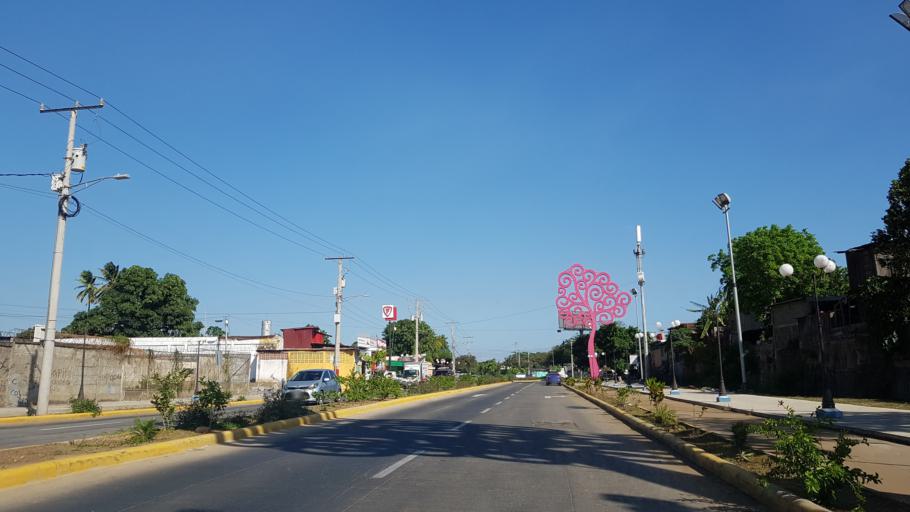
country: NI
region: Managua
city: Managua
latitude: 12.1555
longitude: -86.2650
